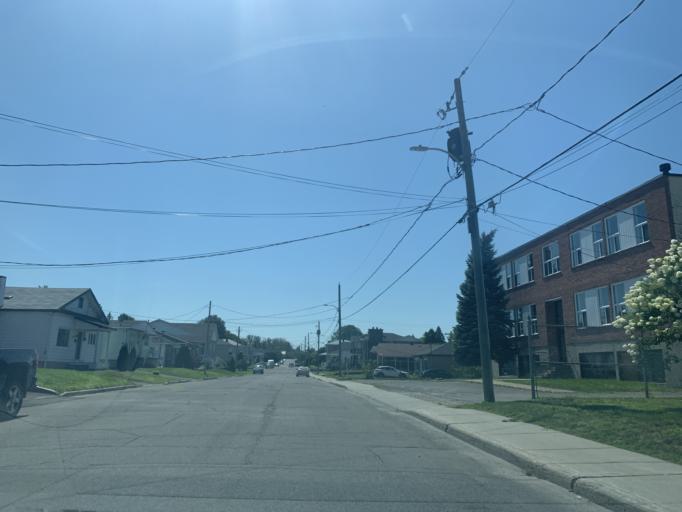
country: CA
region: Ontario
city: Hawkesbury
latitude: 45.6085
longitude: -74.5915
